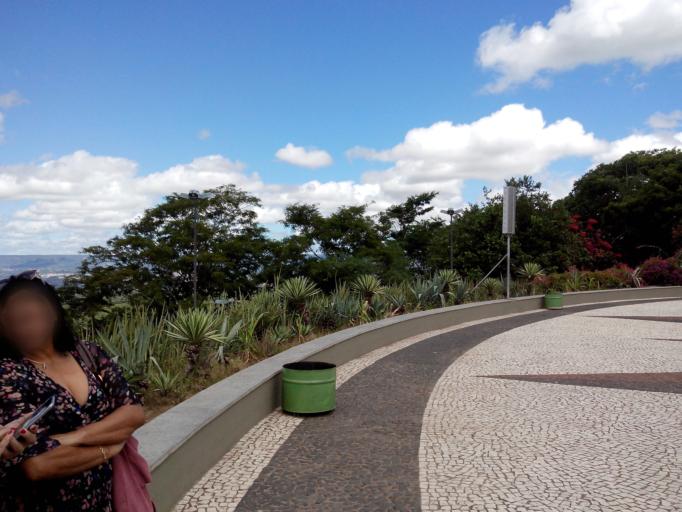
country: BR
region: Ceara
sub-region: Juazeiro Do Norte
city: Juazeiro do Norte
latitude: -7.1800
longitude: -39.3300
